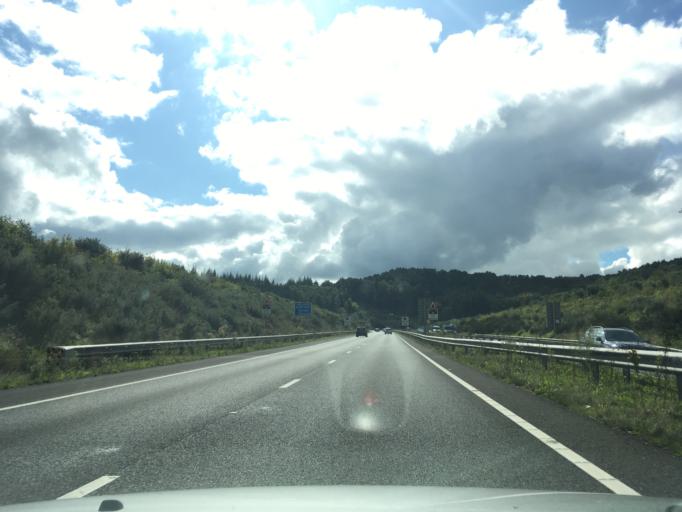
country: GB
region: England
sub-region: Surrey
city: Hindhead
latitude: 51.1250
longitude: -0.7154
